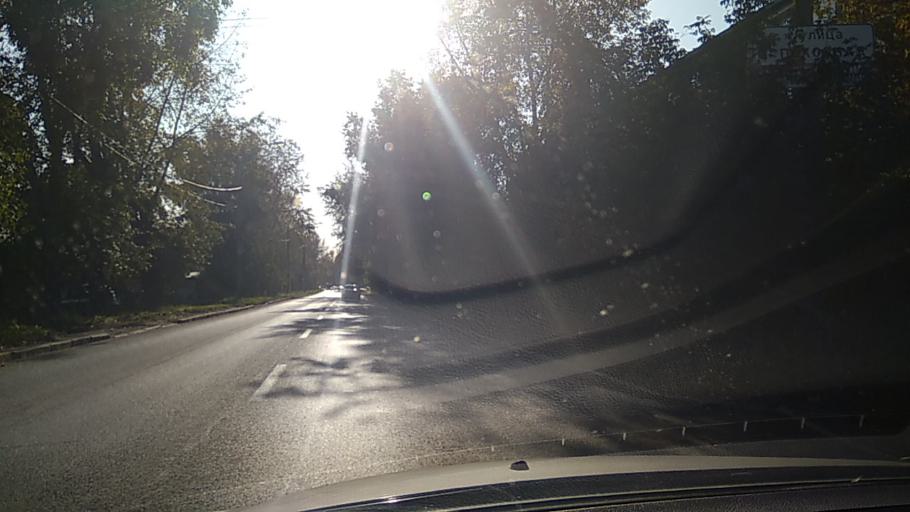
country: RU
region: Sverdlovsk
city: Yekaterinburg
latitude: 56.7756
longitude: 60.6371
